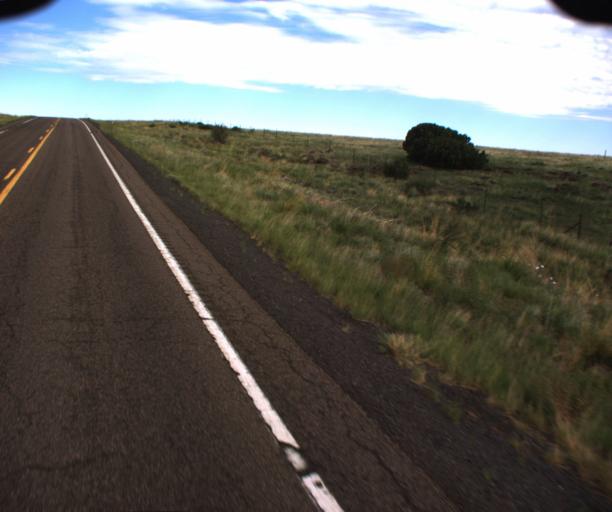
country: US
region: Arizona
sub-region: Apache County
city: Springerville
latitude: 34.2341
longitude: -109.4987
